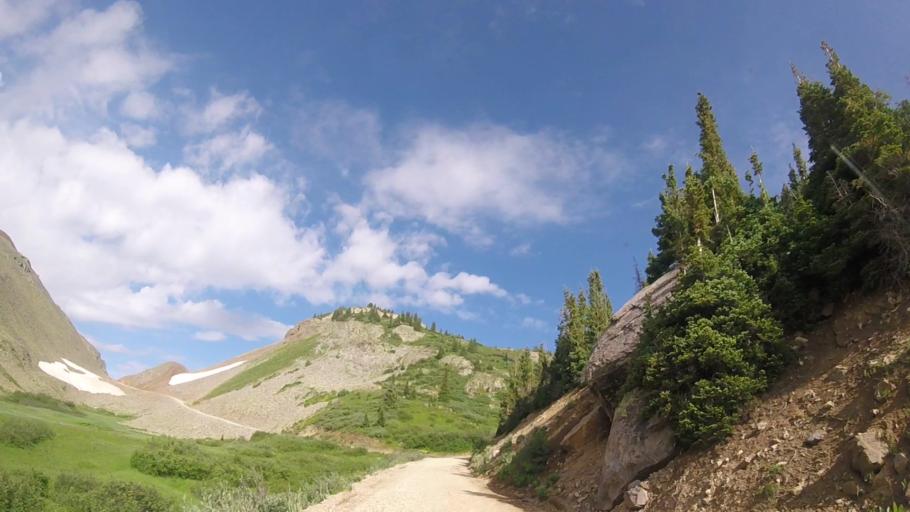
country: US
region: Colorado
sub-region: San Miguel County
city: Telluride
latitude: 37.8513
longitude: -107.7753
